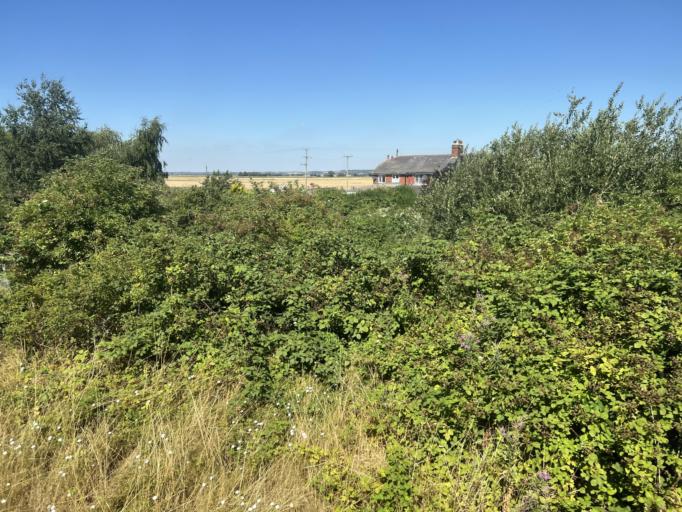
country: GB
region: England
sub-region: Lincolnshire
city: Spilsby
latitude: 53.1096
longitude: 0.1225
